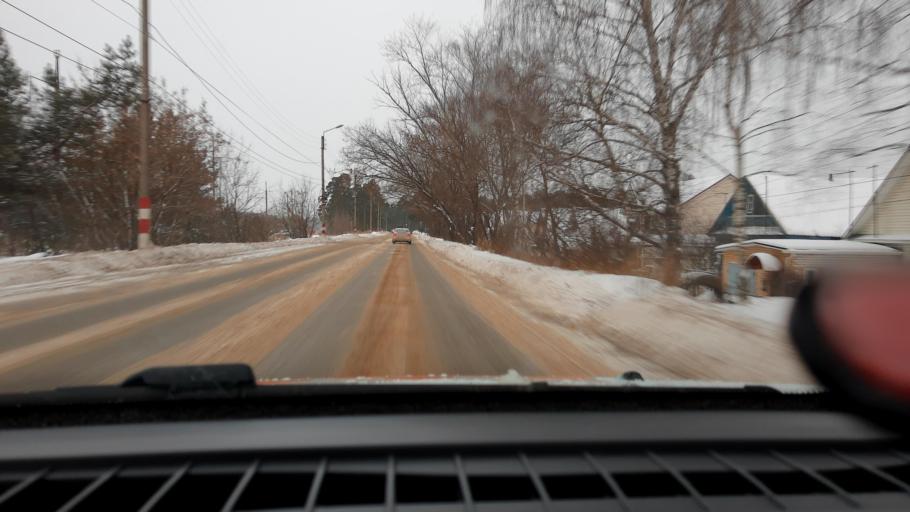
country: RU
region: Nizjnij Novgorod
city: Bor
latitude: 56.3274
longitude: 44.1297
